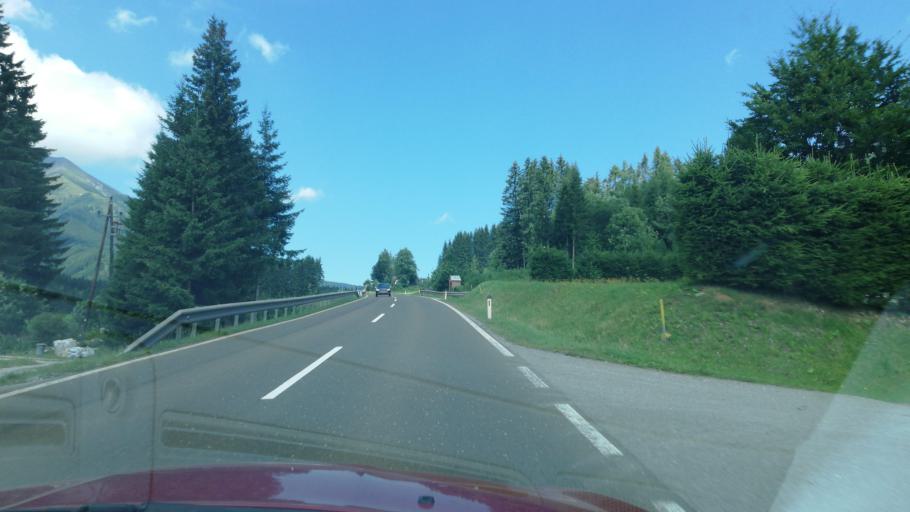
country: AT
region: Styria
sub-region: Politischer Bezirk Murtal
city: Hohentauern
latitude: 47.3979
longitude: 14.4647
